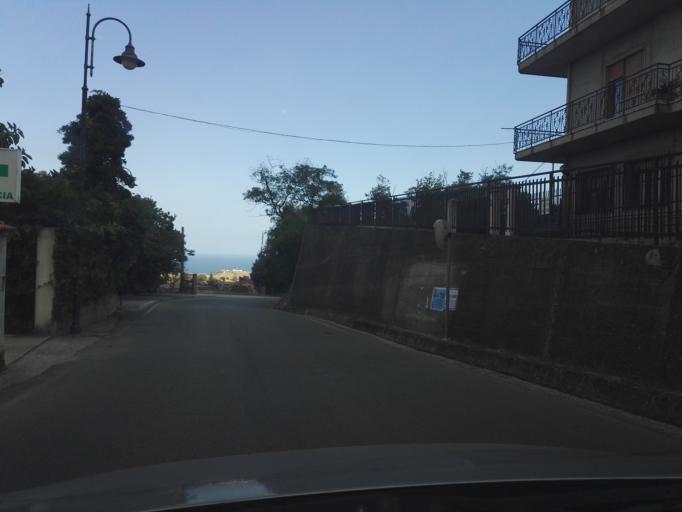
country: IT
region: Calabria
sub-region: Provincia di Reggio Calabria
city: Riace
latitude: 38.4171
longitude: 16.4809
